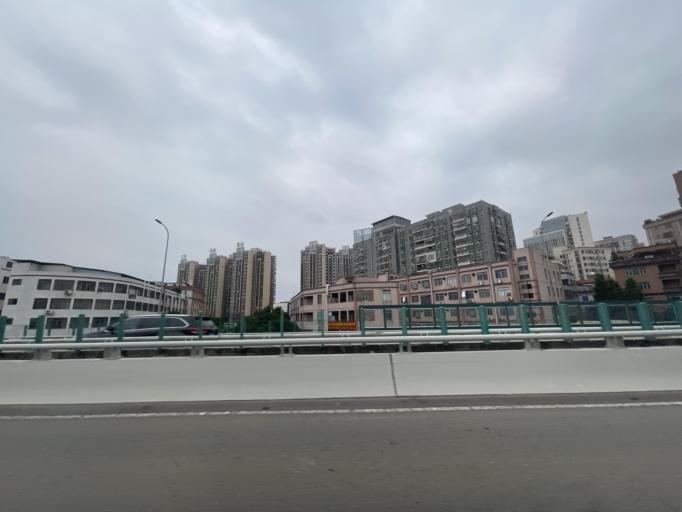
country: CN
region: Guangdong
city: Humen
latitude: 22.8060
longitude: 113.6794
